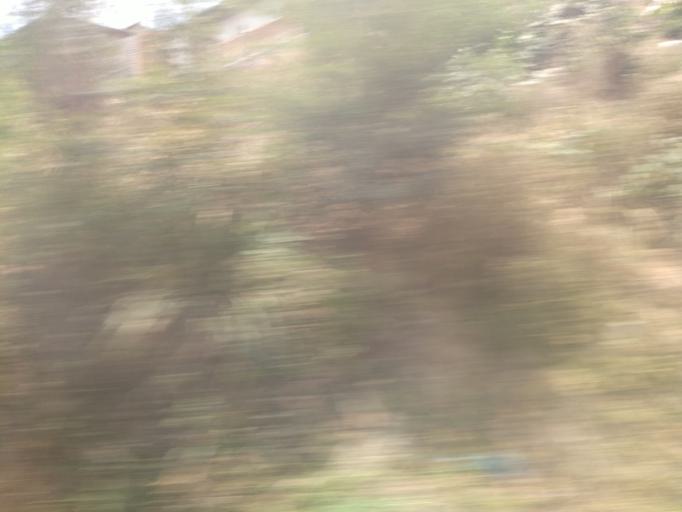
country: TZ
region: Dar es Salaam
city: Dar es Salaam
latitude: -6.8859
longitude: 39.2722
